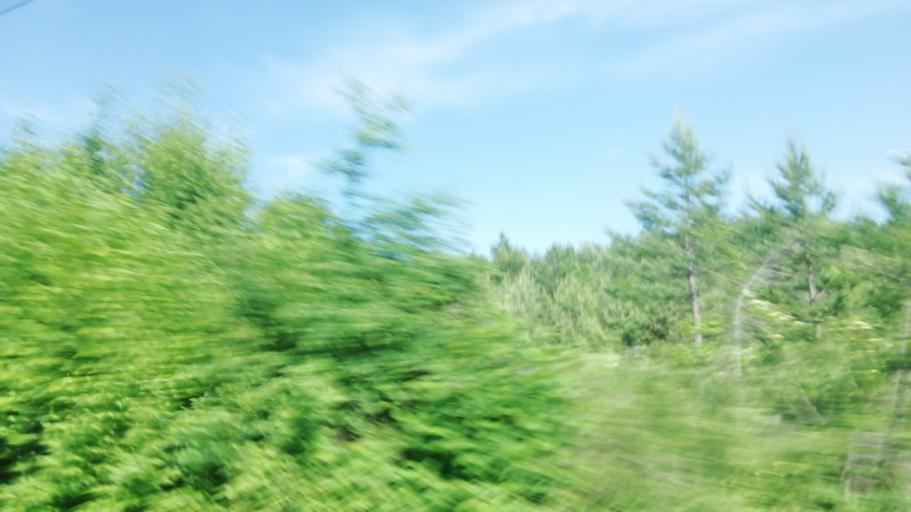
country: TR
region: Karabuk
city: Karabuk
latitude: 41.0838
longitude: 32.5677
